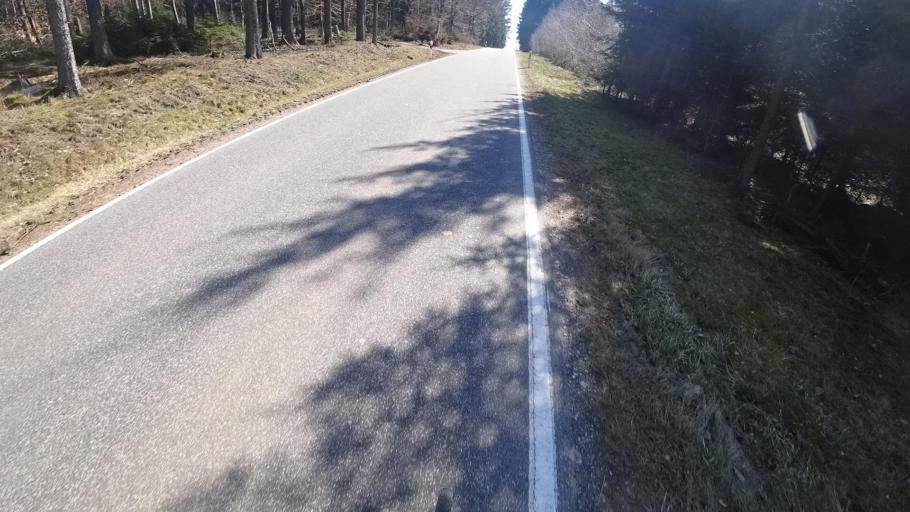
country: DE
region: Rheinland-Pfalz
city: Steinbach
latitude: 50.0347
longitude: 7.6014
